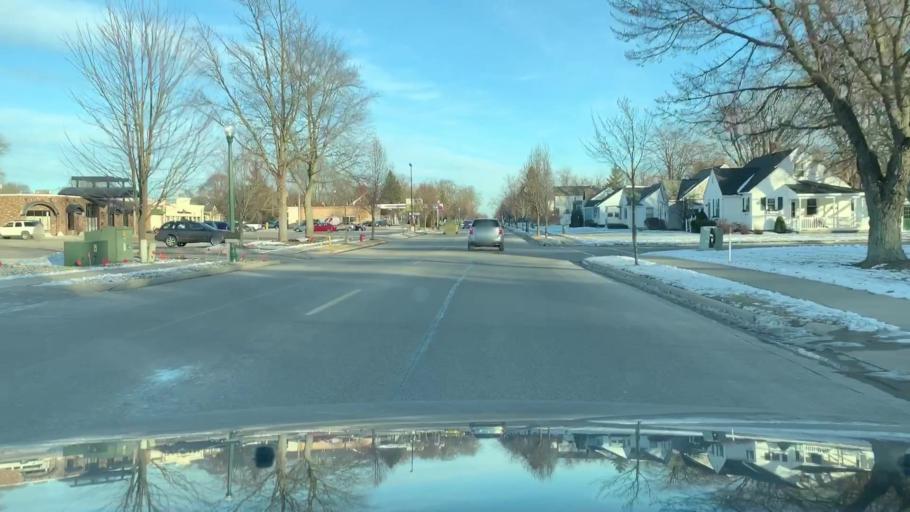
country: US
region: Michigan
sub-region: Ottawa County
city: Zeeland
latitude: 42.8123
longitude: -86.0314
